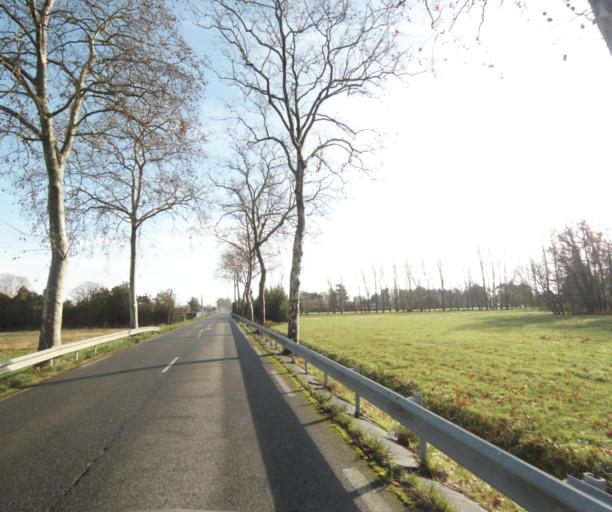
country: FR
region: Midi-Pyrenees
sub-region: Departement du Tarn-et-Garonne
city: Nohic
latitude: 43.8760
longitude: 1.4571
